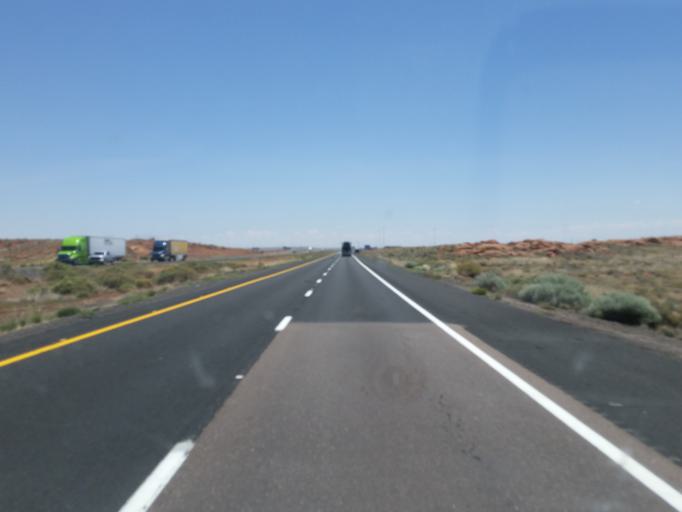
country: US
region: Arizona
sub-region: Coconino County
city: LeChee
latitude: 35.1078
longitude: -111.0159
